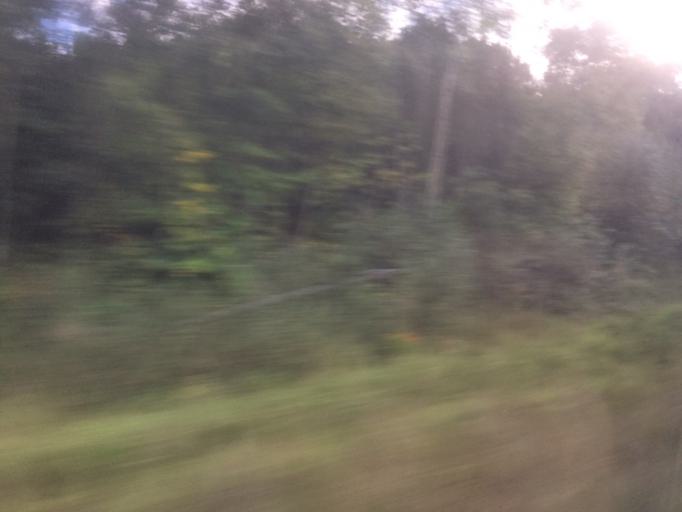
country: GB
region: Scotland
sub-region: North Lanarkshire
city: Cumbernauld
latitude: 55.9697
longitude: -4.0131
